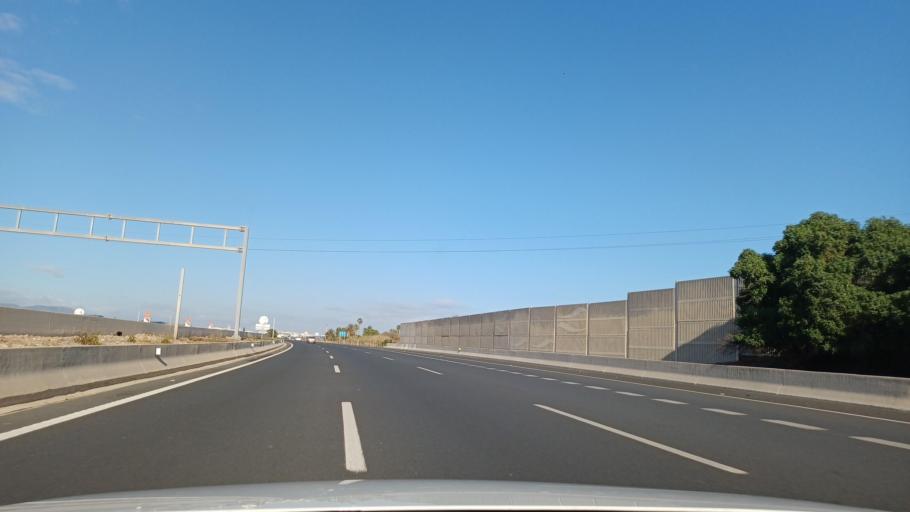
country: ES
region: Valencia
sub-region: Provincia de Valencia
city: Meliana
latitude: 39.5146
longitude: -0.3212
